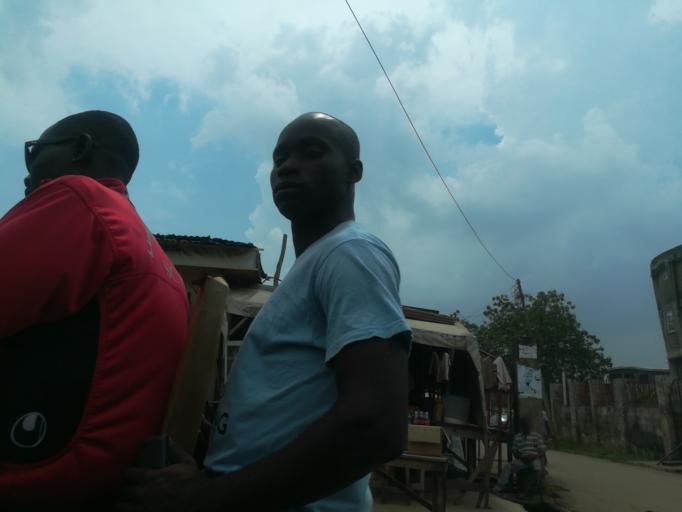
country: NG
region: Oyo
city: Ibadan
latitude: 7.4306
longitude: 3.9216
